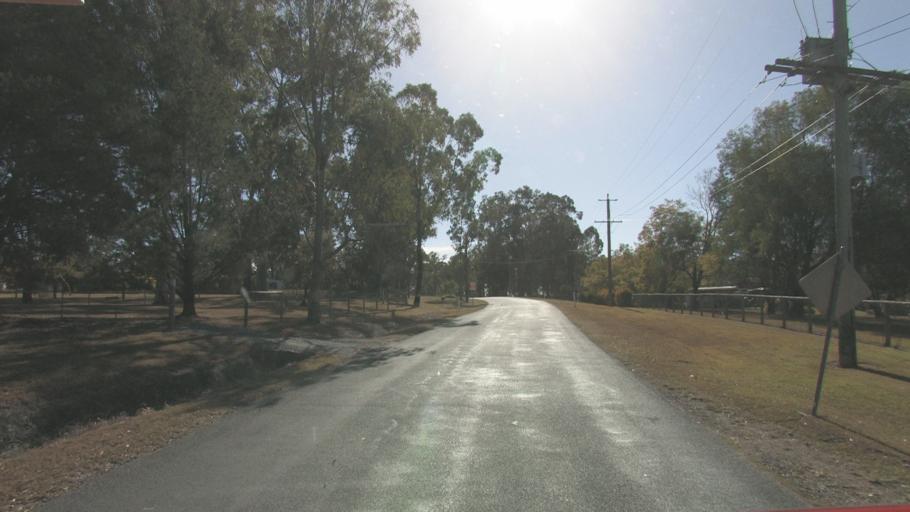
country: AU
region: Queensland
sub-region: Logan
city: Cedar Vale
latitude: -27.8618
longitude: 152.9901
